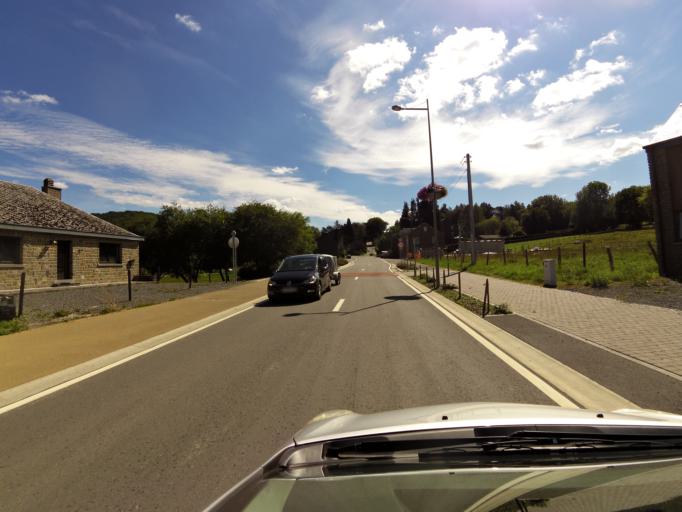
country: BE
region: Wallonia
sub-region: Province du Luxembourg
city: Rendeux
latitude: 50.2317
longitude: 5.5144
